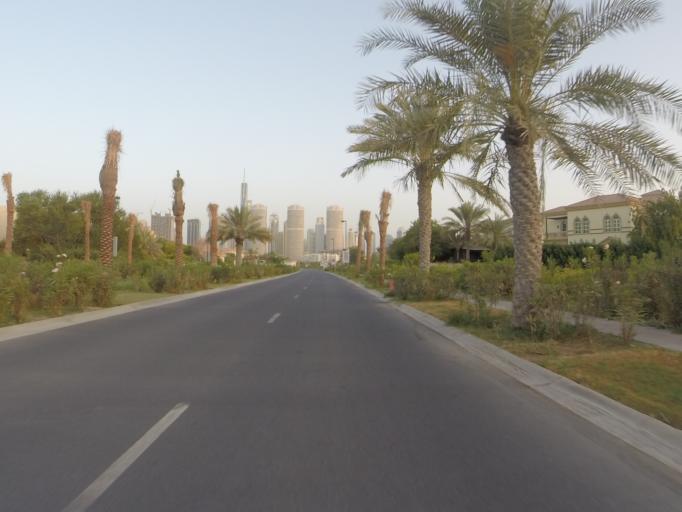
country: AE
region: Dubai
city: Dubai
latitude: 25.0610
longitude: 55.1548
